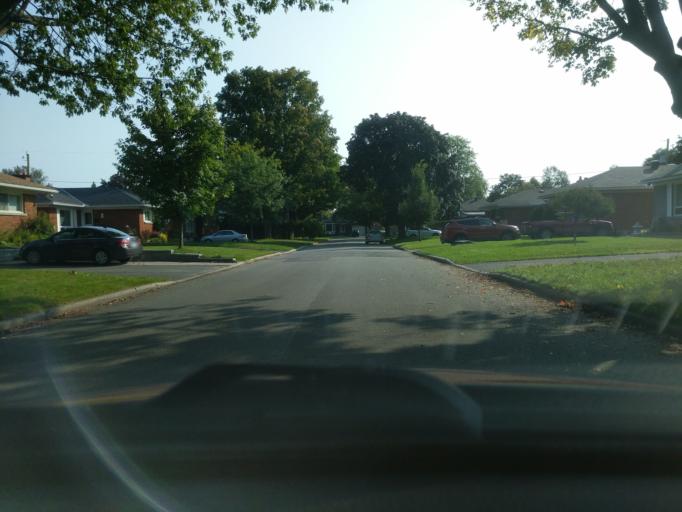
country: CA
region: Ontario
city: Ottawa
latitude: 45.3626
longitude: -75.7537
